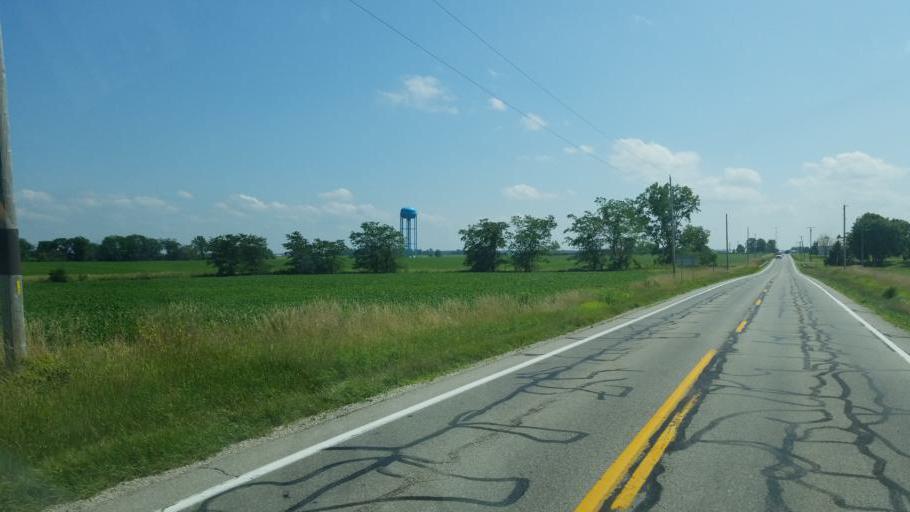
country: US
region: Ohio
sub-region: Huron County
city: Bellevue
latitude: 41.1716
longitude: -82.8378
